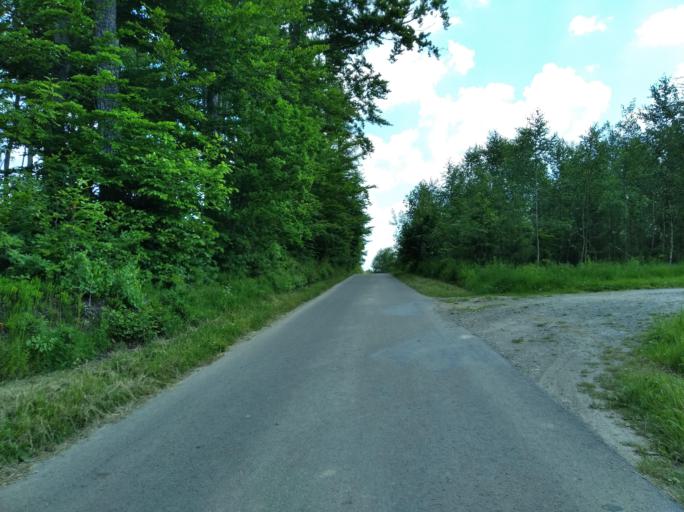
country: PL
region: Subcarpathian Voivodeship
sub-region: Powiat ropczycko-sedziszowski
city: Zagorzyce
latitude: 49.9664
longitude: 21.7124
